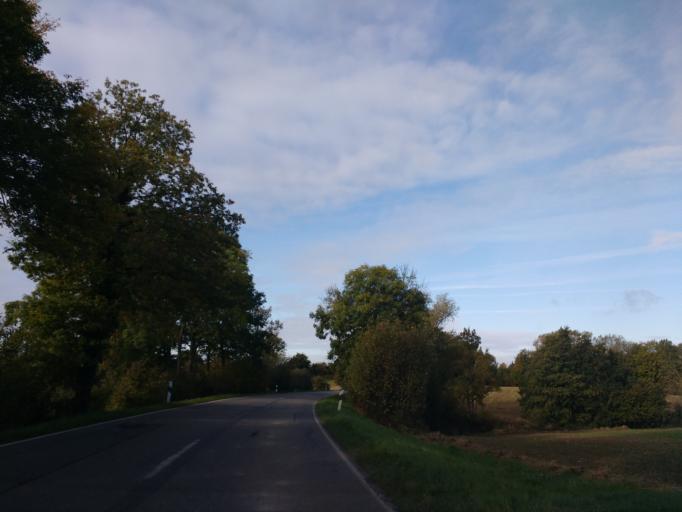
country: DE
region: Schleswig-Holstein
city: Wangels
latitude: 54.2597
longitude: 10.7145
